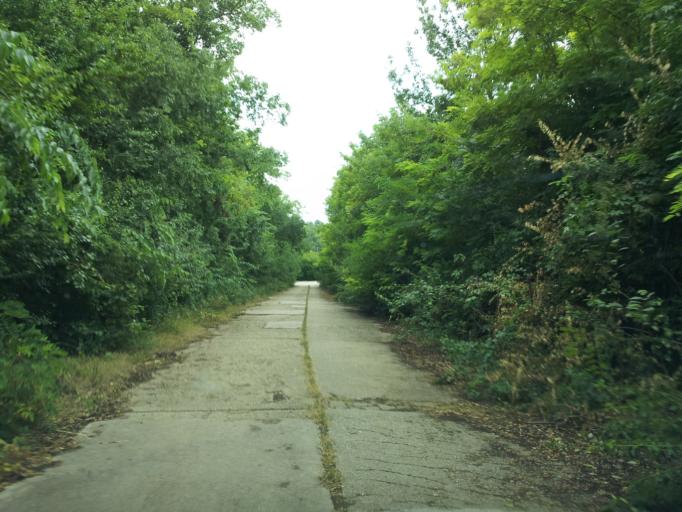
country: HU
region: Fejer
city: Enying
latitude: 46.9160
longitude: 18.2283
